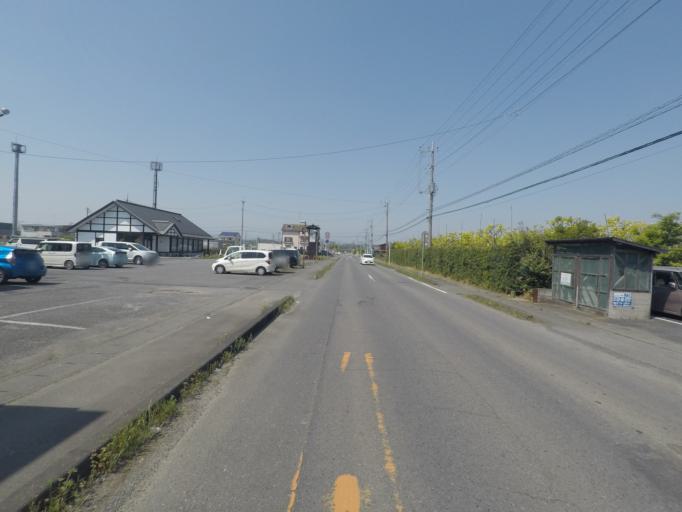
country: JP
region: Ibaraki
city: Naka
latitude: 36.0884
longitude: 140.1859
